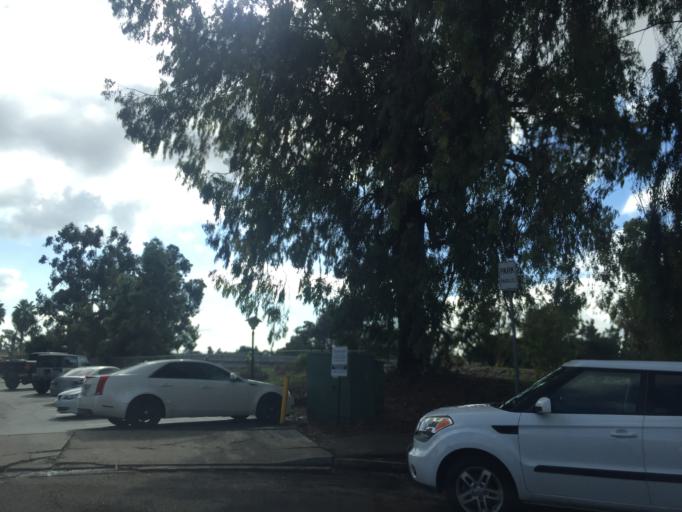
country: US
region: California
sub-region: San Diego County
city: La Jolla
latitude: 32.8029
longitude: -117.2221
